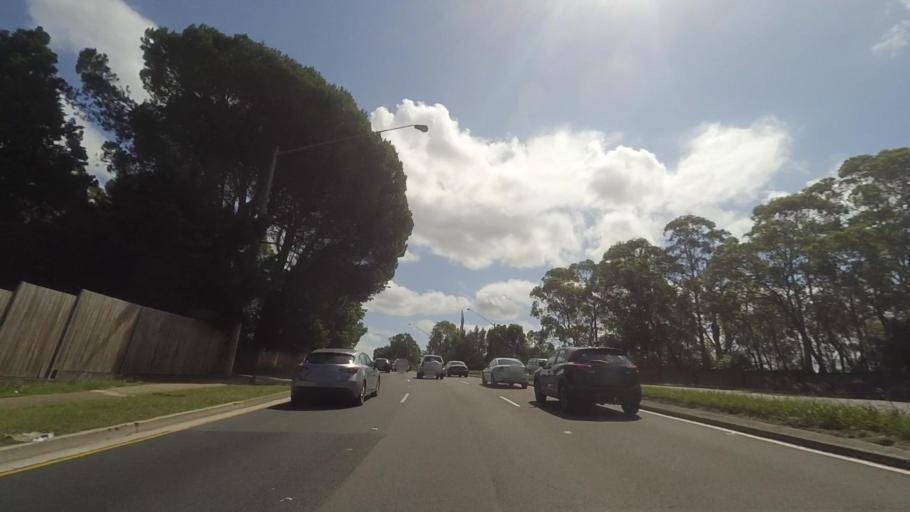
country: AU
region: New South Wales
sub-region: Ku-ring-gai
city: Normanhurst
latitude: -33.7235
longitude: 151.0910
